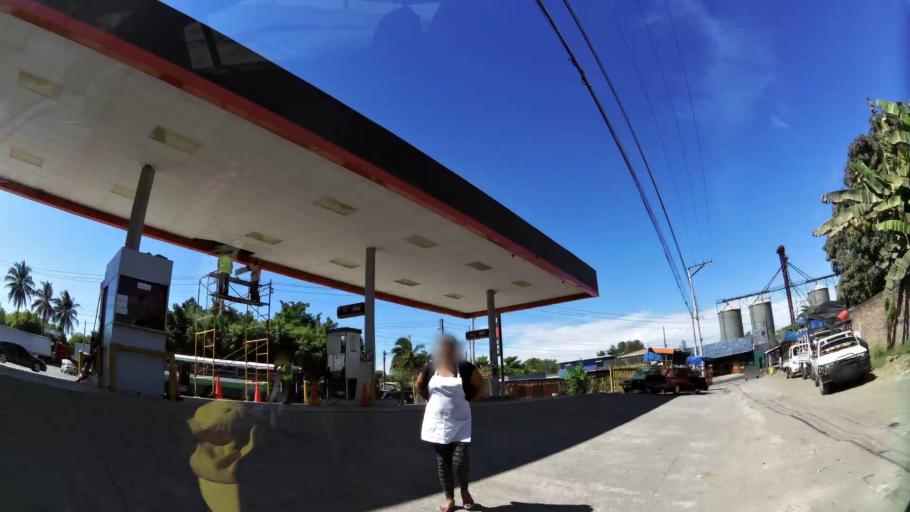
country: SV
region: La Libertad
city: Ciudad Arce
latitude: 13.7808
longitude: -89.3722
